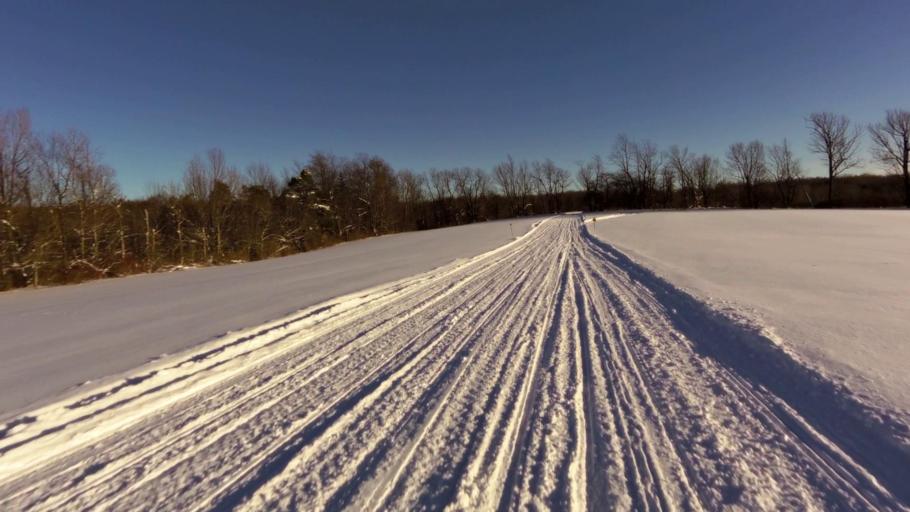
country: US
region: New York
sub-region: Chautauqua County
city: Mayville
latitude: 42.2398
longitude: -79.3929
